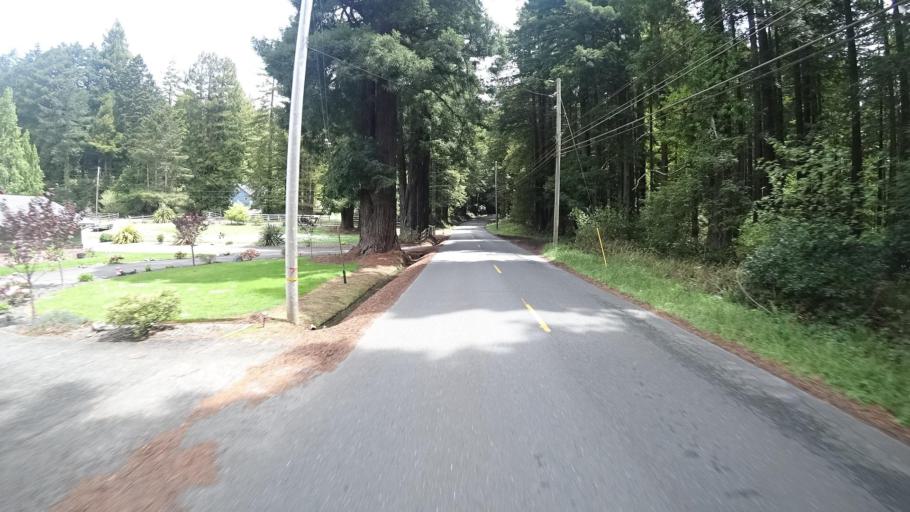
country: US
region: California
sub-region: Humboldt County
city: Myrtletown
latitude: 40.7880
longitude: -124.0811
